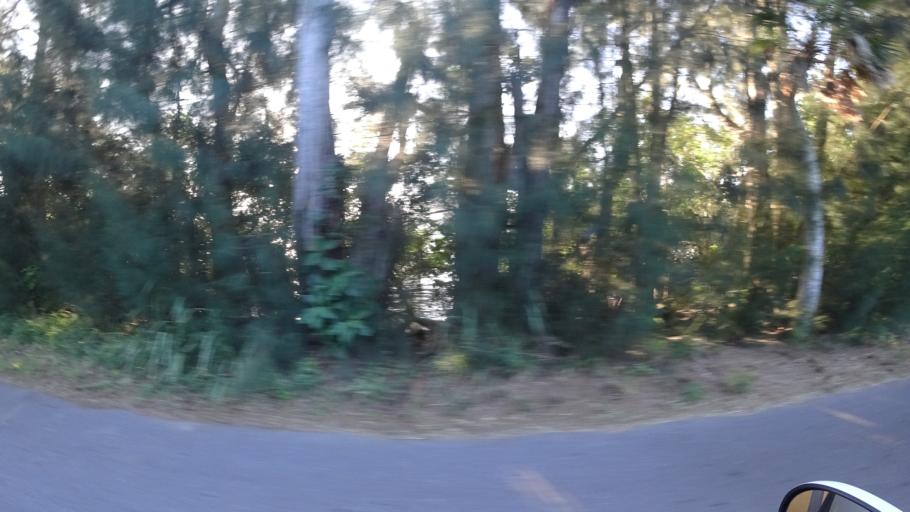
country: US
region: Florida
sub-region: Manatee County
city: Memphis
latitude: 27.5682
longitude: -82.5838
